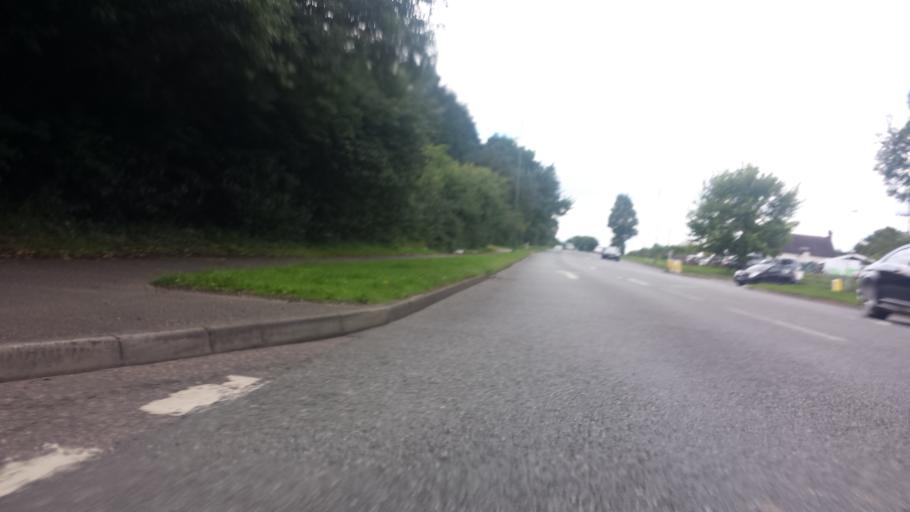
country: GB
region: England
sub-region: Greater London
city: Bexley
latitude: 51.4124
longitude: 0.1378
